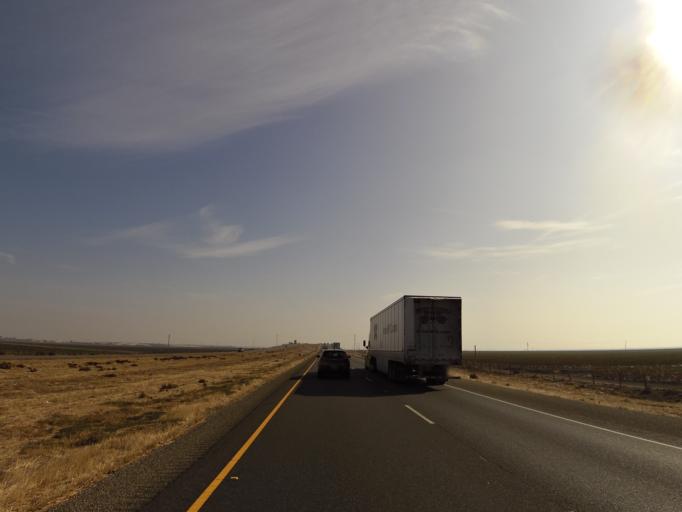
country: US
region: California
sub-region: Kern County
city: Greenfield
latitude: 35.1846
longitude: -119.1364
